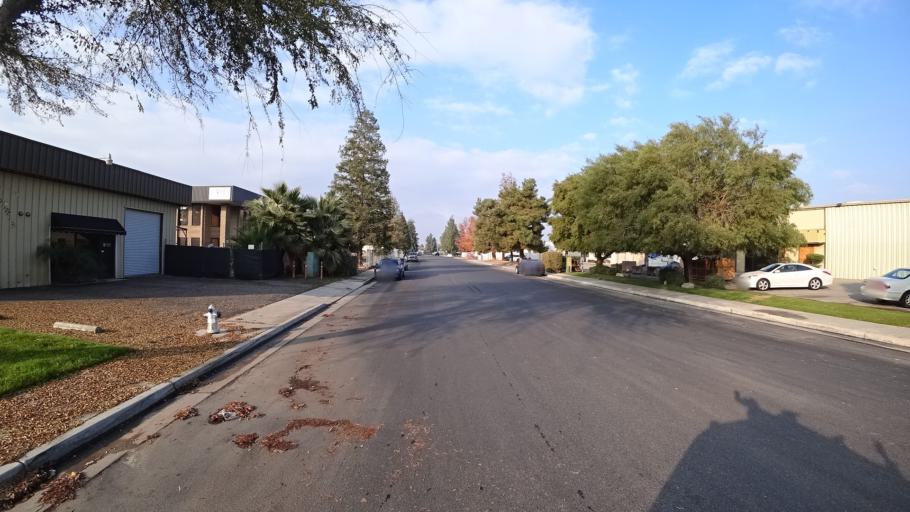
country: US
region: California
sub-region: Kern County
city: Bakersfield
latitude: 35.3165
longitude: -119.0616
